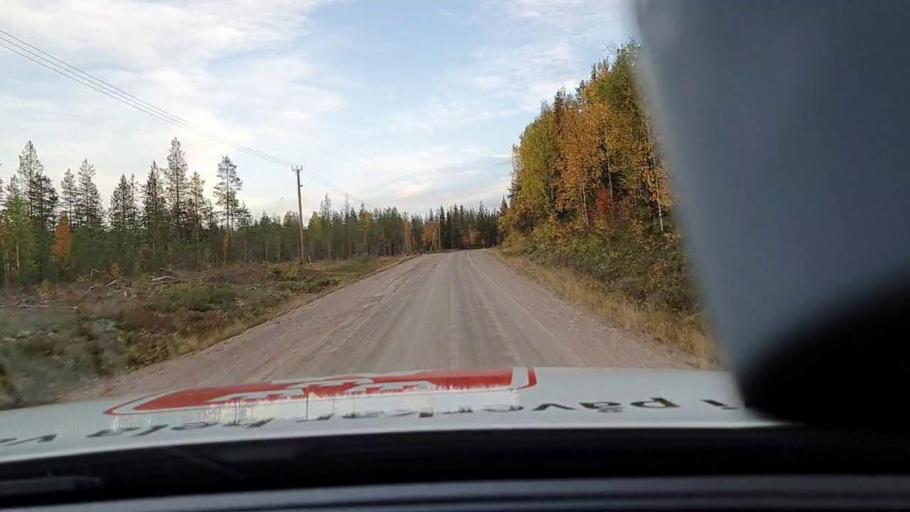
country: SE
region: Norrbotten
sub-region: Overkalix Kommun
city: OEverkalix
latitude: 66.3219
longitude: 22.6338
